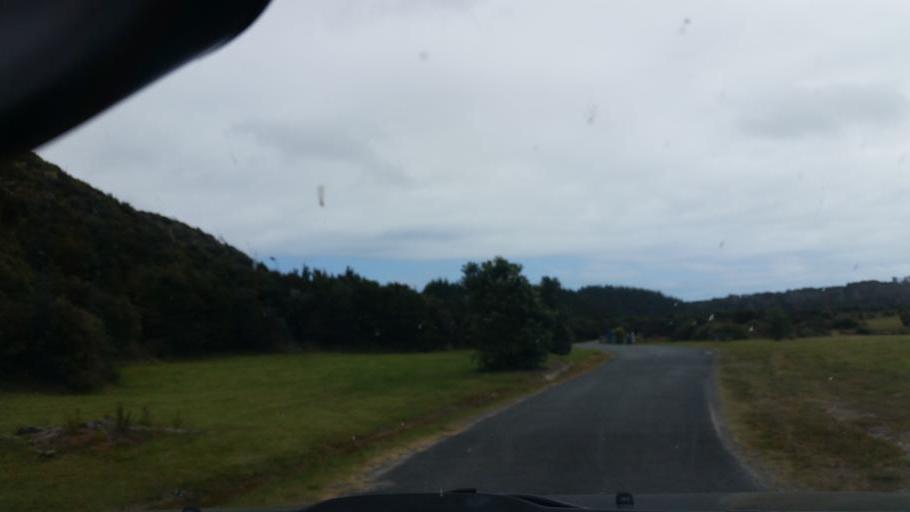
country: NZ
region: Northland
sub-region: Kaipara District
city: Dargaville
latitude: -35.8104
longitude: 173.6624
